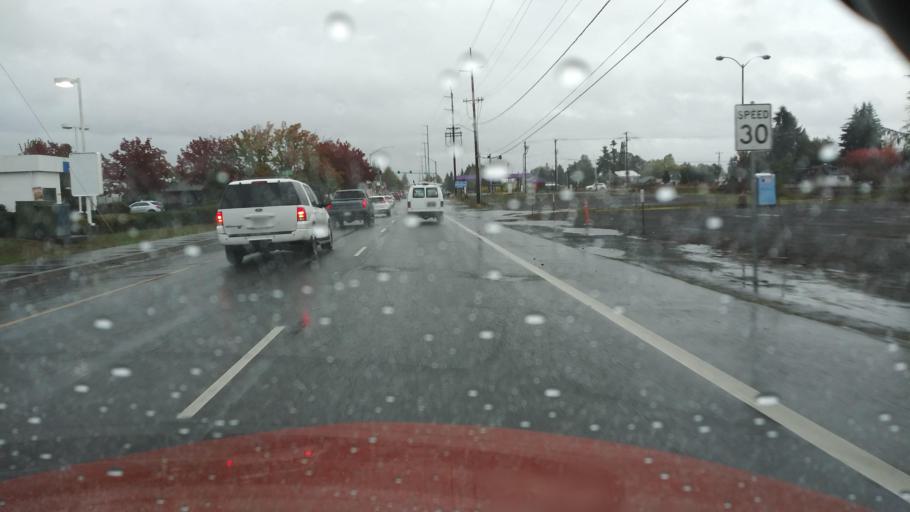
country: US
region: Oregon
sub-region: Washington County
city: Cornelius
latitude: 45.5200
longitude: -123.0618
